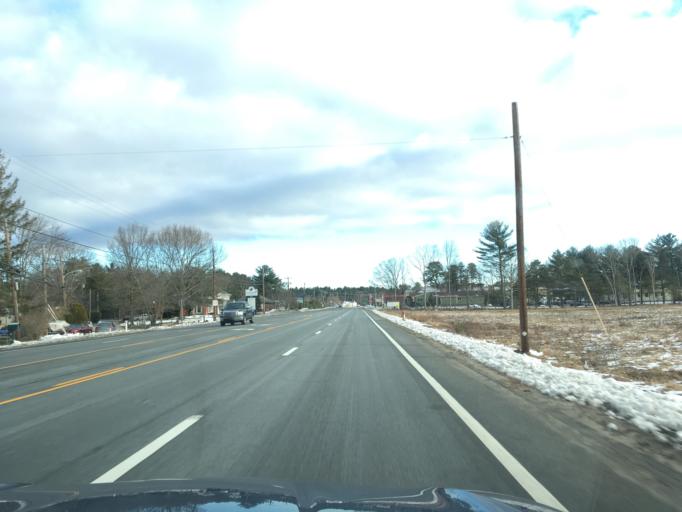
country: US
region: Rhode Island
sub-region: Kent County
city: West Greenwich
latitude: 41.6651
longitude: -71.6016
